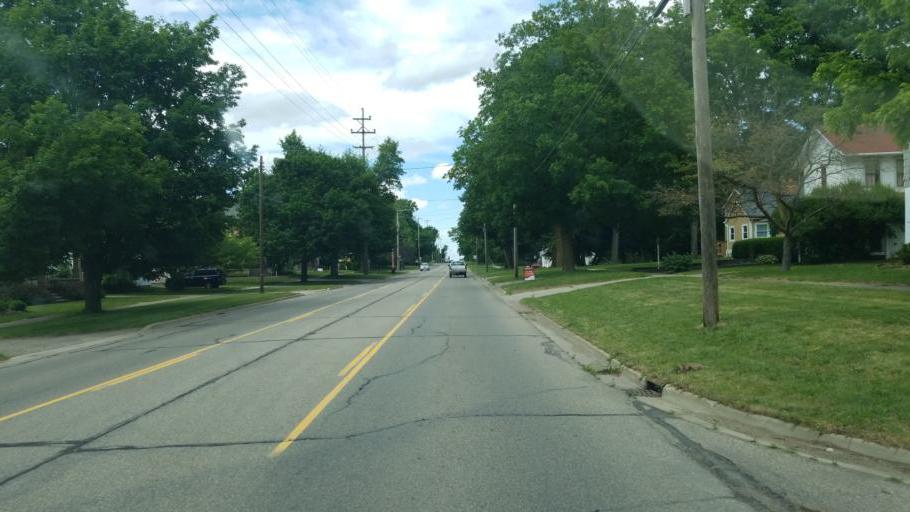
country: US
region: Michigan
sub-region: Eaton County
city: Charlotte
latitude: 42.5739
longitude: -84.8359
